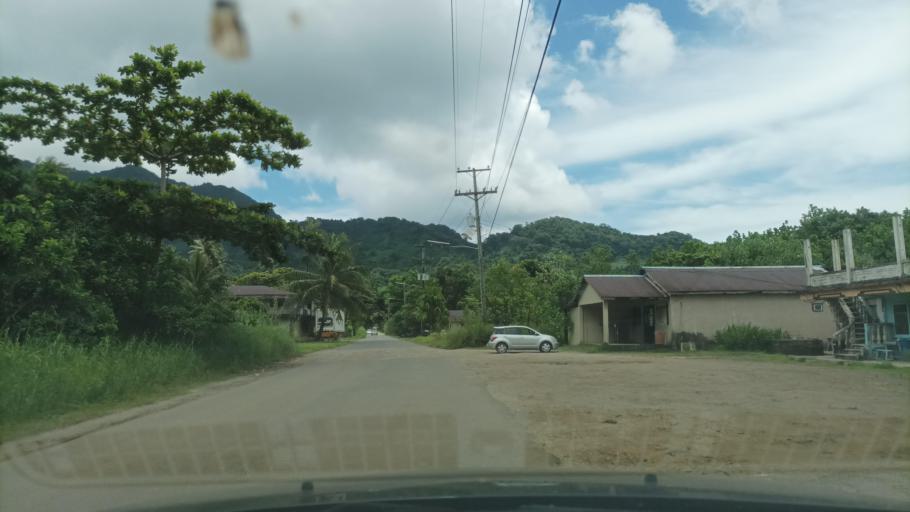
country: FM
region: Kosrae
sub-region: Lelu Municipality
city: Tofol
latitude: 5.3280
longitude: 163.0085
